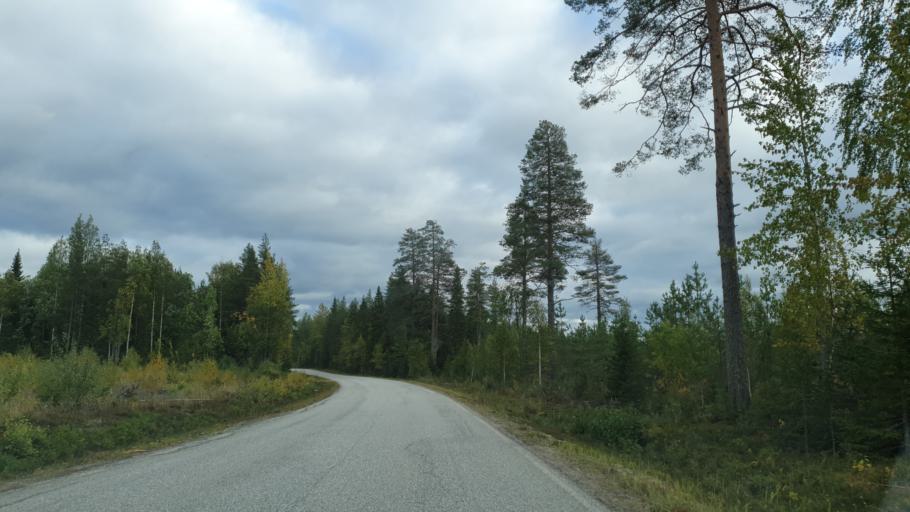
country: FI
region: Kainuu
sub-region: Kehys-Kainuu
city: Kuhmo
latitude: 63.9483
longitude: 29.7602
